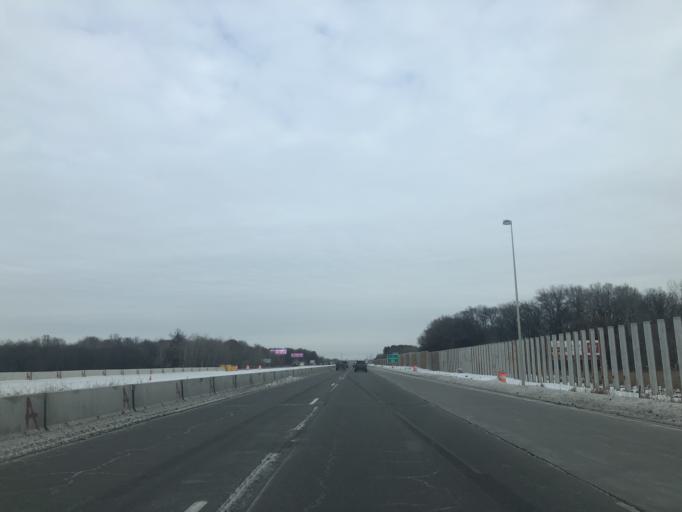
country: US
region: Minnesota
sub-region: Anoka County
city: Lexington
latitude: 45.1463
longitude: -93.1811
